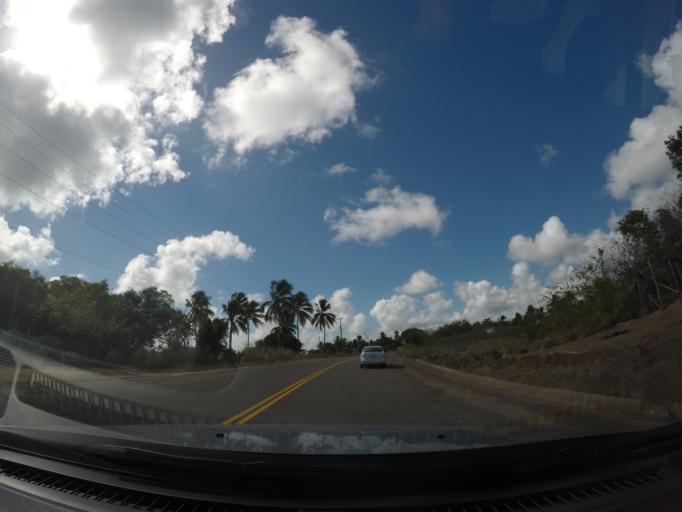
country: BR
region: Paraiba
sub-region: Pitimbu
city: Pitimbu
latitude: -7.4516
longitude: -34.8362
